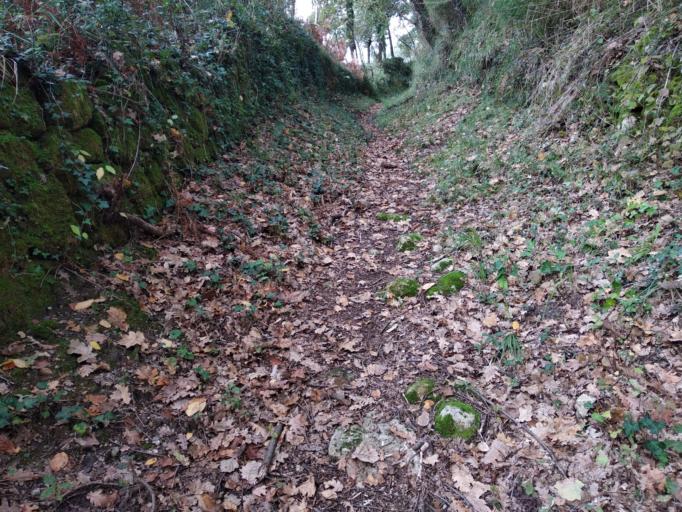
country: IT
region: Calabria
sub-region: Provincia di Cosenza
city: Altilia
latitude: 39.1269
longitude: 16.2483
